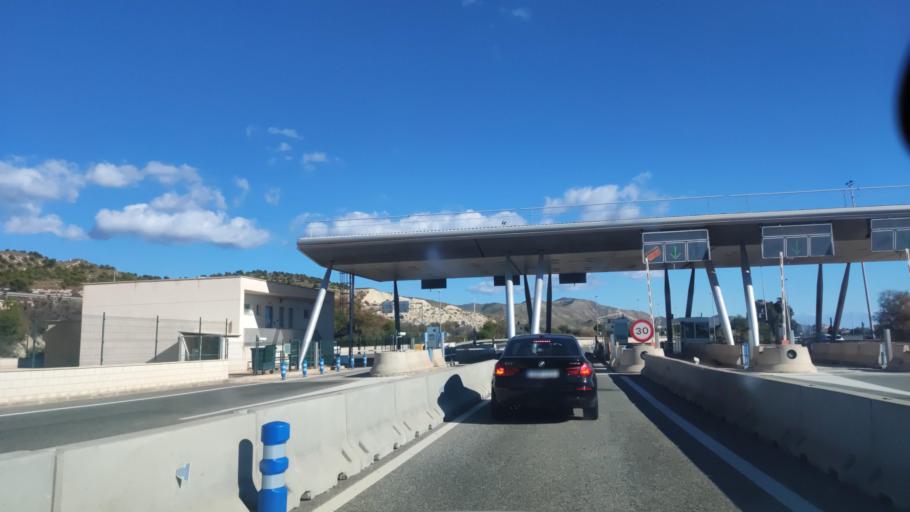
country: ES
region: Valencia
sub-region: Provincia de Alicante
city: el Campello
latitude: 38.4404
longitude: -0.4009
